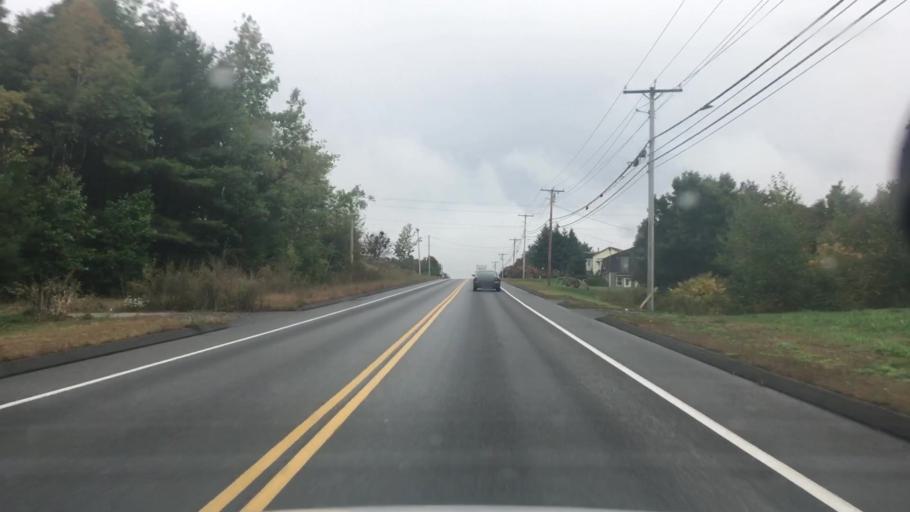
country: US
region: Maine
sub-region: Kennebec County
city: Augusta
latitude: 44.3636
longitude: -69.7874
